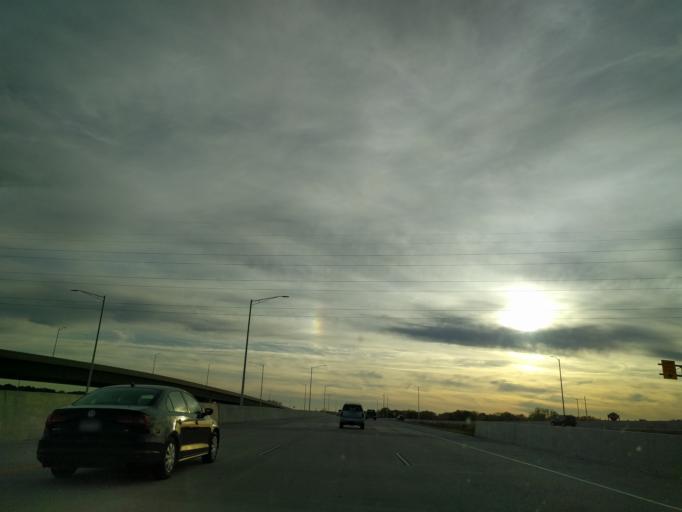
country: US
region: Wisconsin
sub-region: Brown County
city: Howard
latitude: 44.5594
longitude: -88.0567
